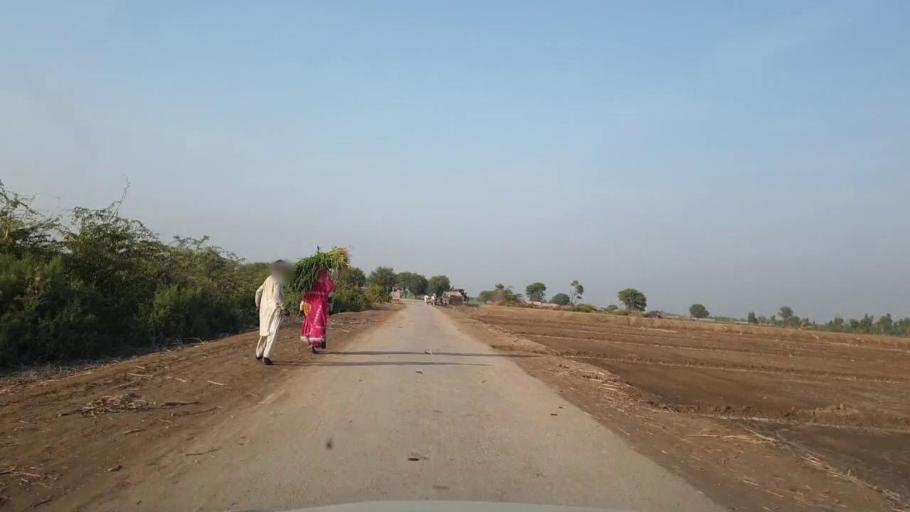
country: PK
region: Sindh
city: Pithoro
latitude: 25.6754
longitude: 69.2044
